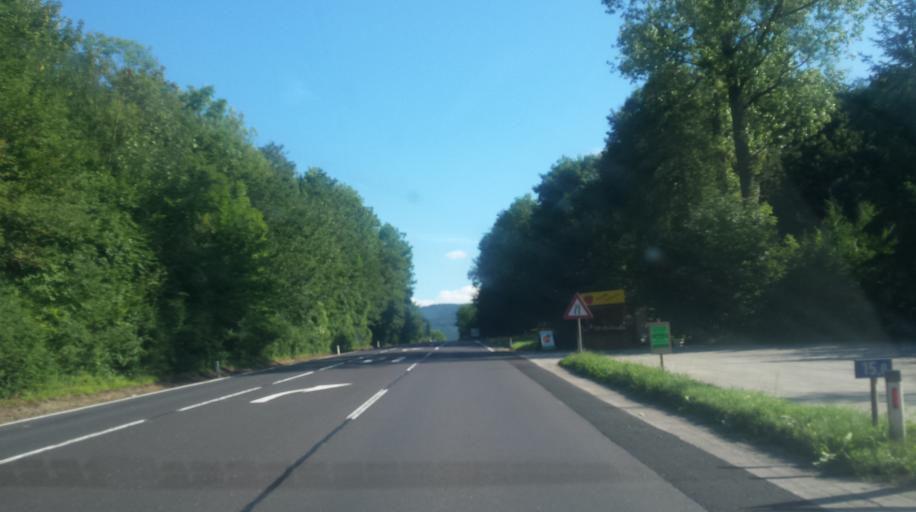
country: AT
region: Upper Austria
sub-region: Politischer Bezirk Vocklabruck
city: Attnang-Puchheim
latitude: 47.9792
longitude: 13.7009
